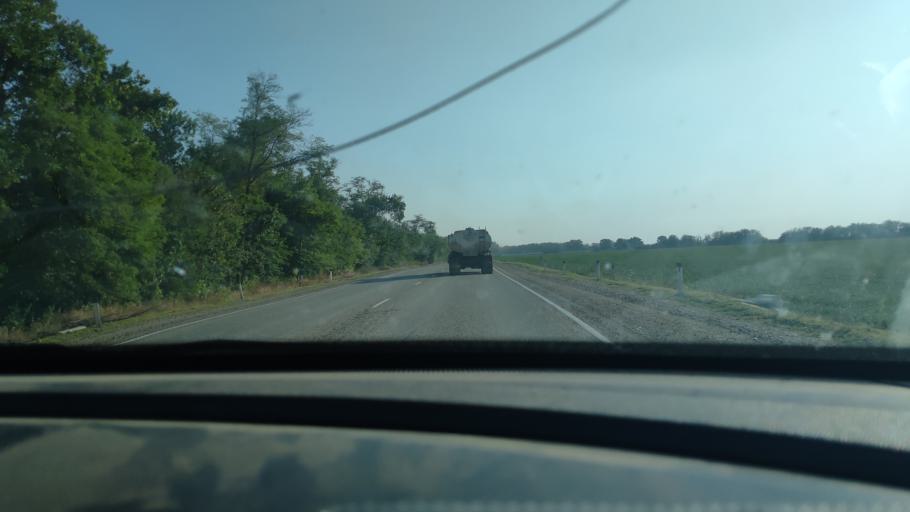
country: RU
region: Krasnodarskiy
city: Starominskaya
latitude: 46.4576
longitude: 39.0348
